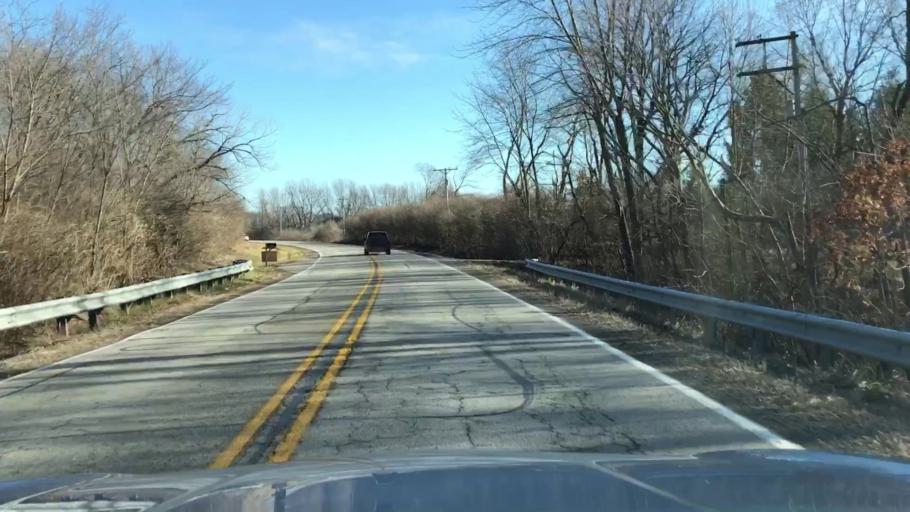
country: US
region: Illinois
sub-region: McLean County
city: Lexington
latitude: 40.6458
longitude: -88.8369
